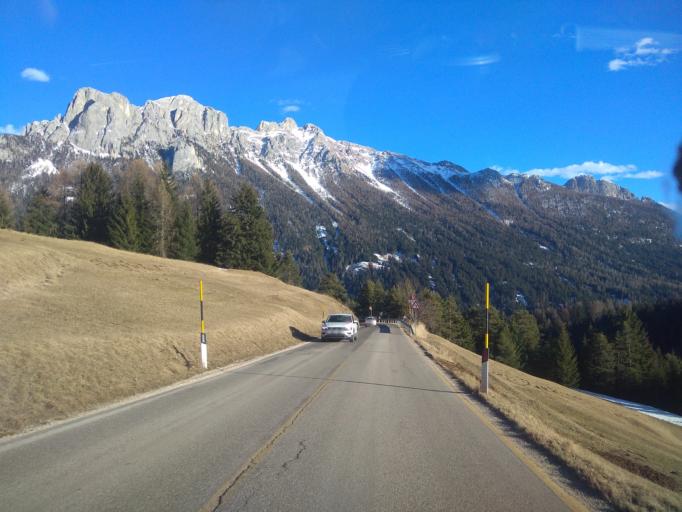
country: IT
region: Trentino-Alto Adige
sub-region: Provincia di Trento
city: Vigo di Fassa
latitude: 46.4125
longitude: 11.6633
